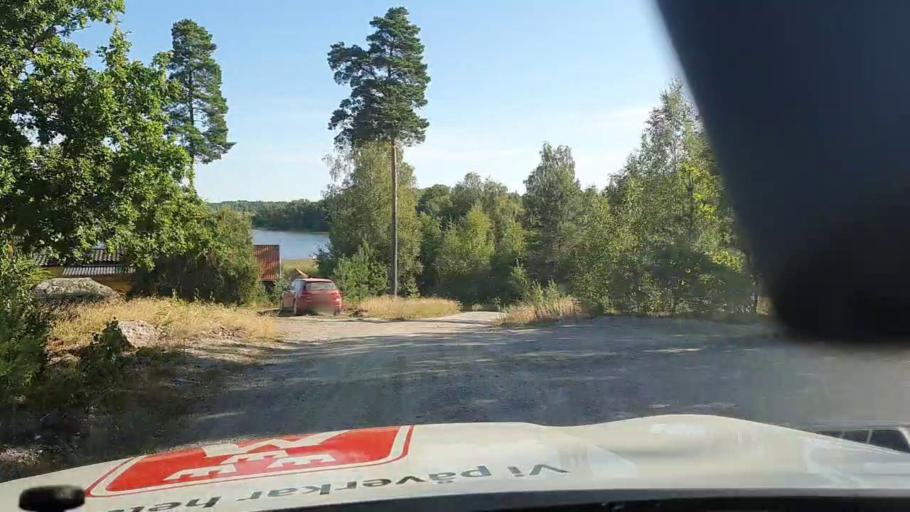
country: SE
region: Soedermanland
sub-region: Eskilstuna Kommun
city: Eskilstuna
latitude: 59.4598
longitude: 16.6491
